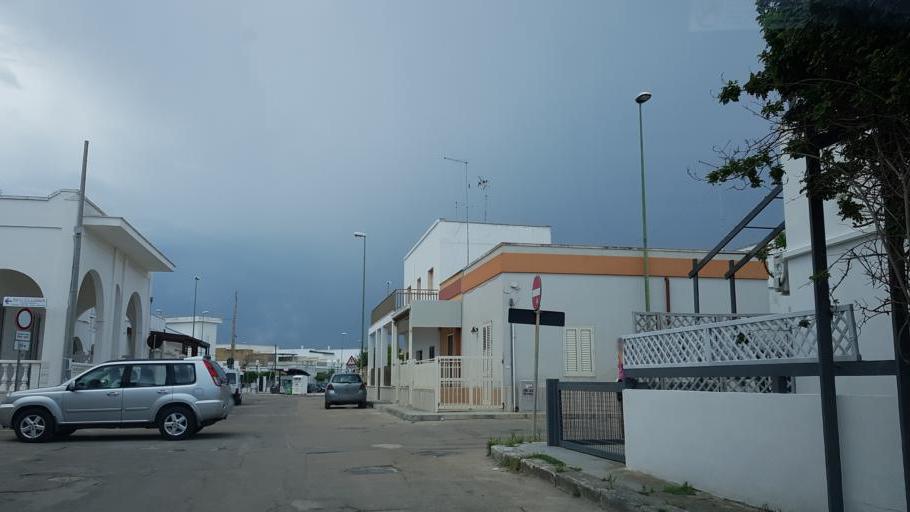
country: IT
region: Apulia
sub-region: Provincia di Lecce
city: Porto Cesareo
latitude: 40.2873
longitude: 17.8508
